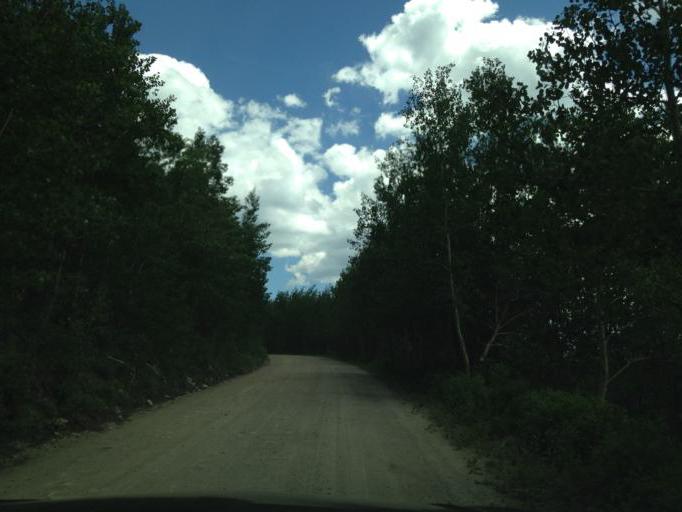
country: US
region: Colorado
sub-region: Park County
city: Fairplay
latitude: 39.3439
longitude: -105.9210
